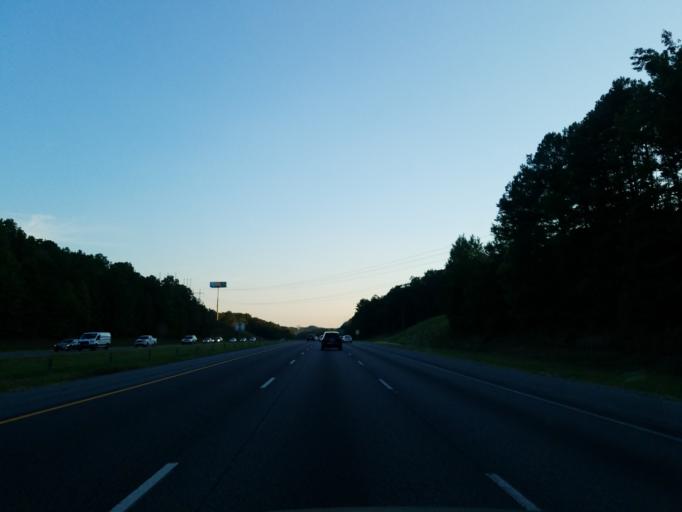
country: US
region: Georgia
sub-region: Bartow County
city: Emerson
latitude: 34.1332
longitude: -84.7381
